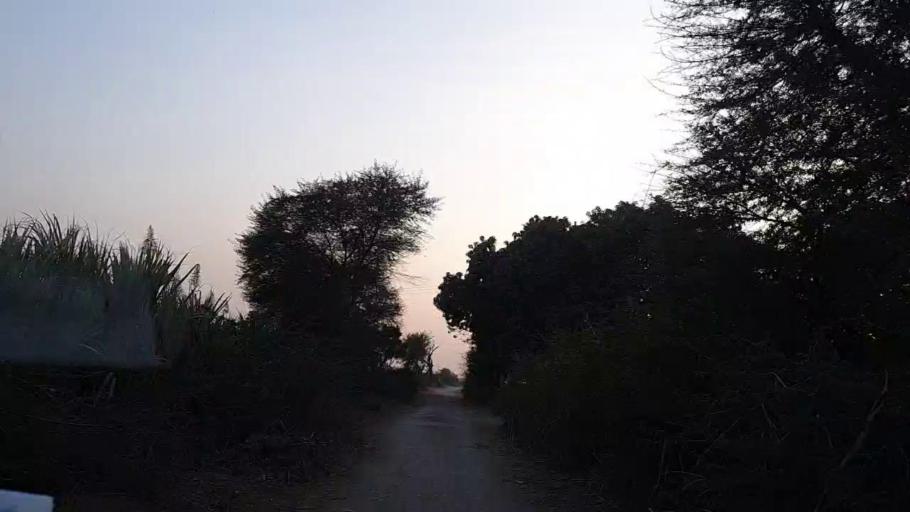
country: PK
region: Sindh
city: Tando Ghulam Ali
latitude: 25.1725
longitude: 68.9274
